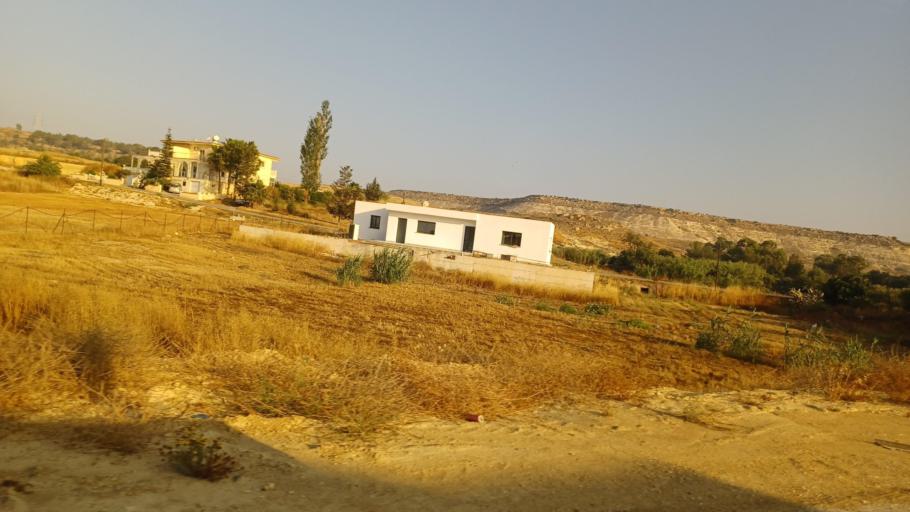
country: CY
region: Larnaka
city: Pyla
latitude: 35.0069
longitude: 33.6863
